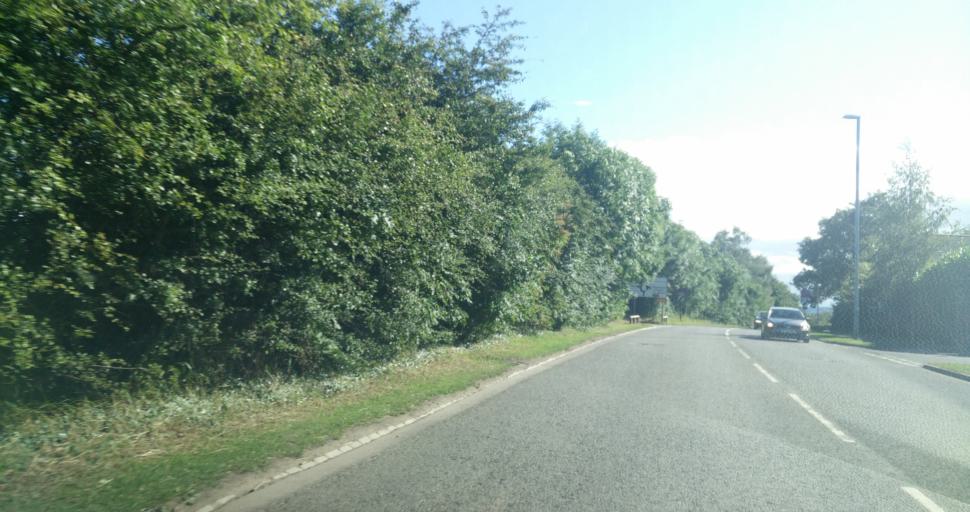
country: GB
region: England
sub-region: County Durham
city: Durham
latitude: 54.7541
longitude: -1.5891
